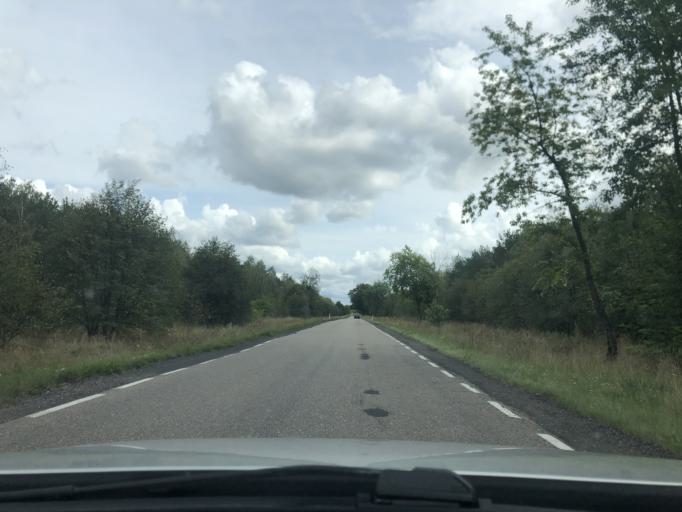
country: PL
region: Greater Poland Voivodeship
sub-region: Powiat czarnkowsko-trzcianecki
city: Wielen
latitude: 52.9032
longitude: 16.1271
